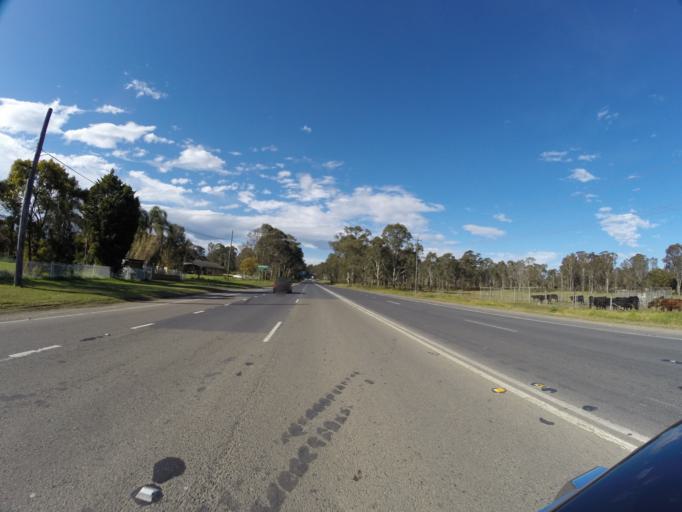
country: AU
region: New South Wales
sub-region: Fairfield
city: Cecil Park
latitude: -33.8805
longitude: 150.8093
